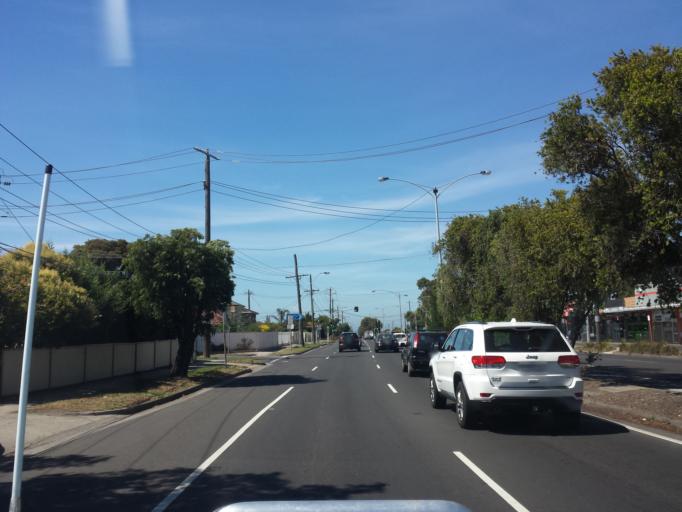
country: AU
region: Victoria
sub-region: Hobsons Bay
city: Altona North
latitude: -37.8259
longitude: 144.8492
